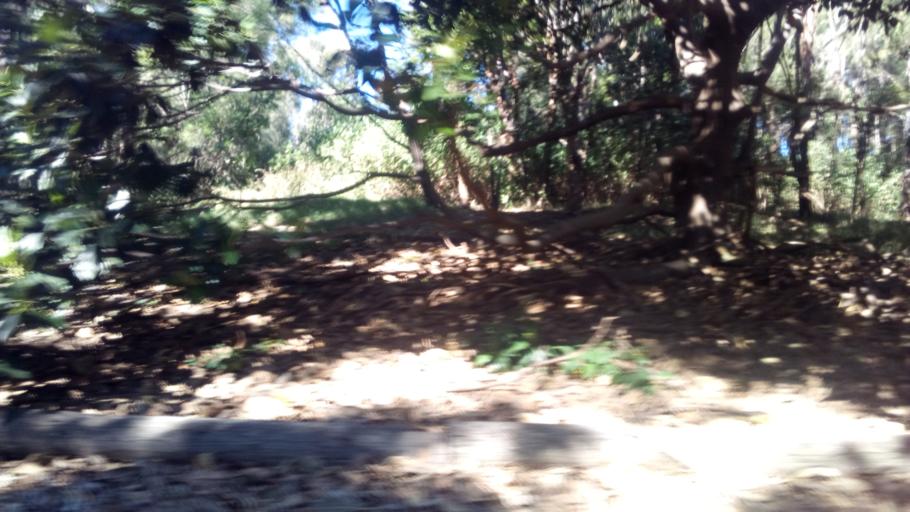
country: AU
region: New South Wales
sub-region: Wollongong
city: Coniston
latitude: -34.4403
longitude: 150.8923
